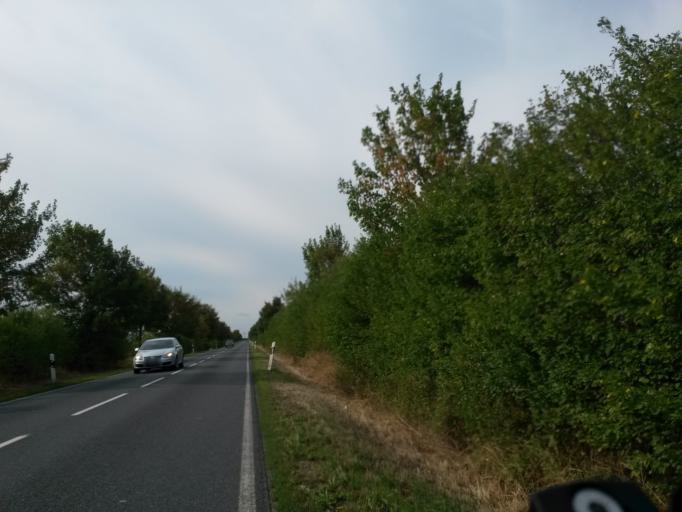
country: DE
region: Saxony-Anhalt
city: Stendal
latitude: 52.5375
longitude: 11.8842
